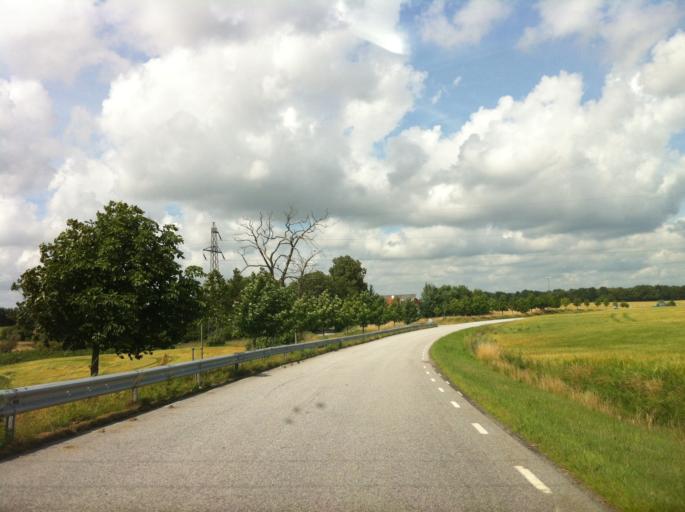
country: SE
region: Skane
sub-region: Trelleborgs Kommun
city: Anderslov
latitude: 55.4343
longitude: 13.3869
